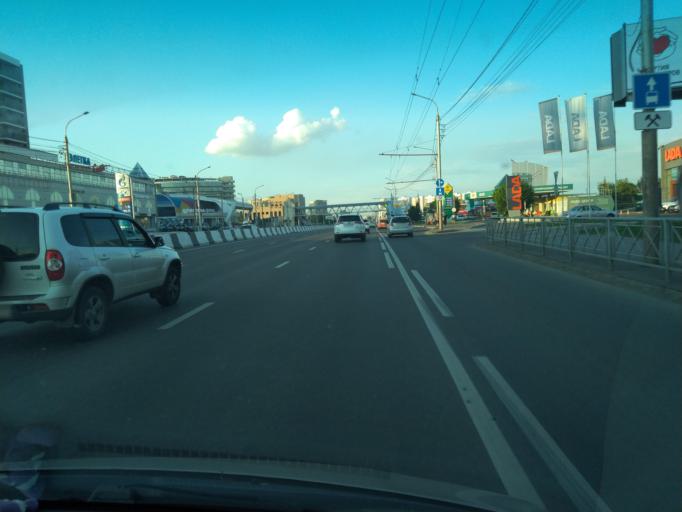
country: RU
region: Krasnoyarskiy
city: Krasnoyarsk
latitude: 56.0340
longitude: 92.9248
